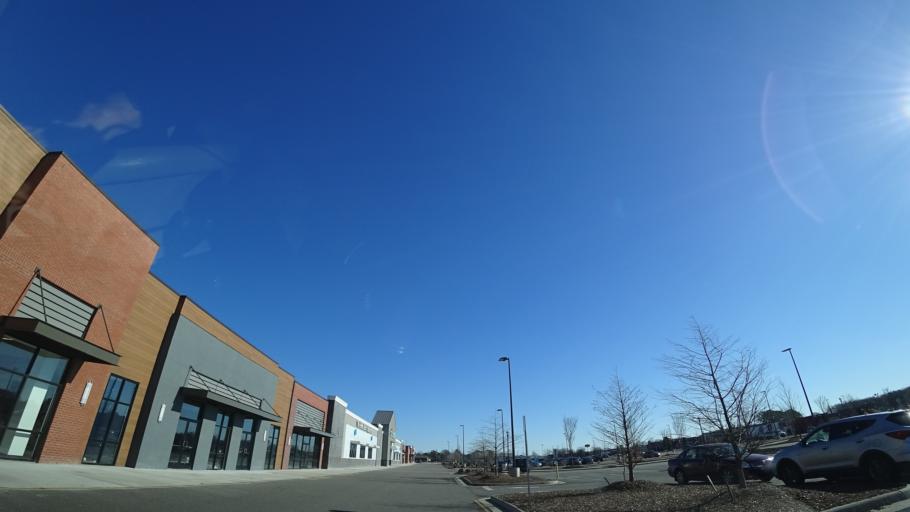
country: US
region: Virginia
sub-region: City of Hampton
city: Hampton
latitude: 37.0439
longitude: -76.3868
